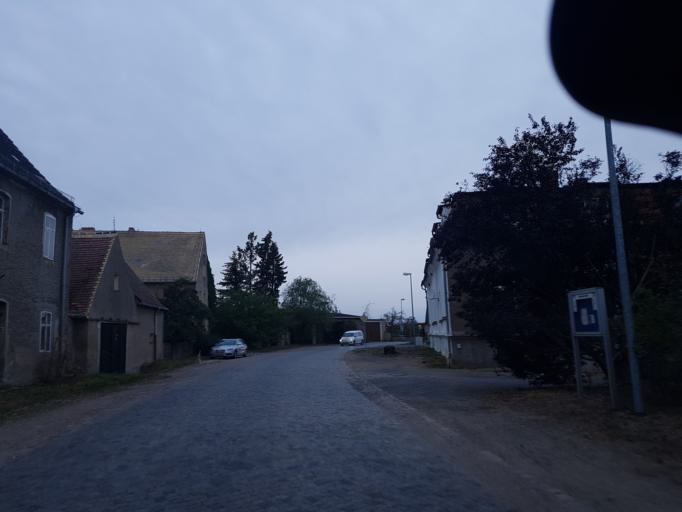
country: DE
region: Saxony
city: Belgern
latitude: 51.4934
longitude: 13.1832
